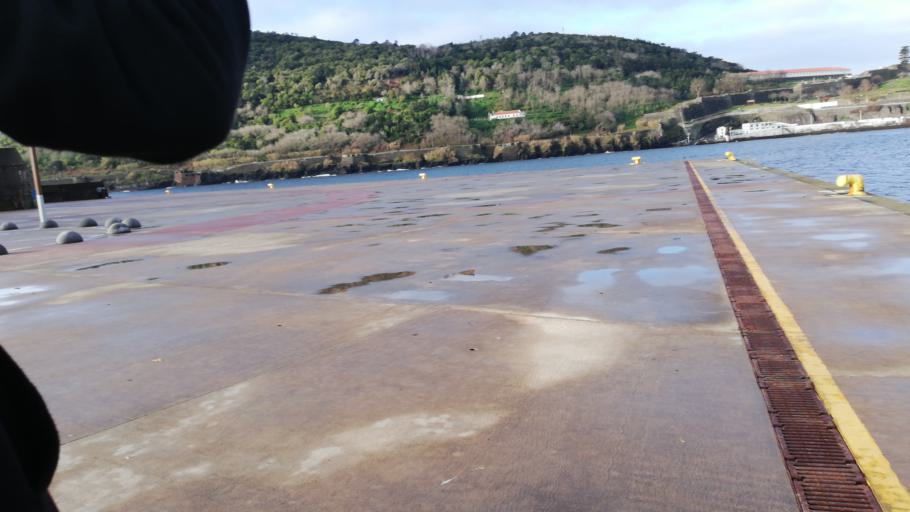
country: PT
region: Azores
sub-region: Angra do Heroismo
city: Angra do Heroismo
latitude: 38.6516
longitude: -27.2149
